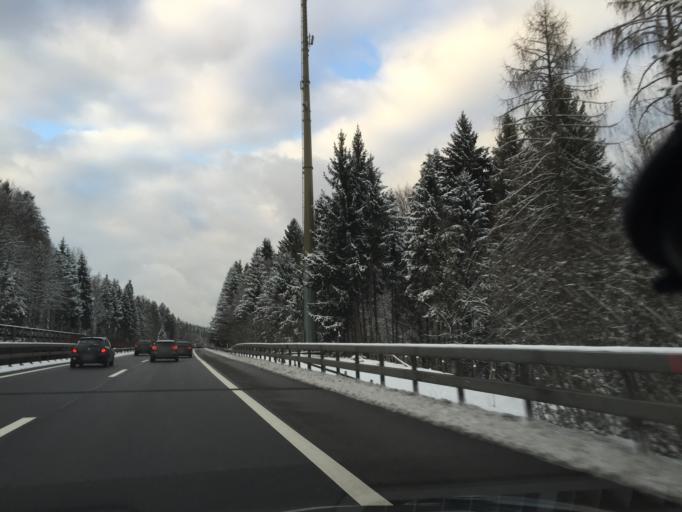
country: CH
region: Zurich
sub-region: Bezirk Horgen
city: Horgen / Scheller-Stockerstrasse
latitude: 47.2616
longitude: 8.5785
